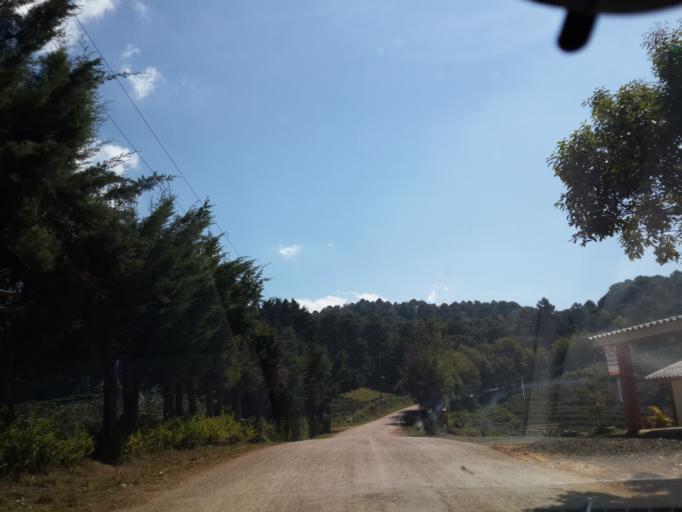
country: TH
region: Chiang Mai
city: Fang
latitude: 19.9327
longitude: 99.0427
